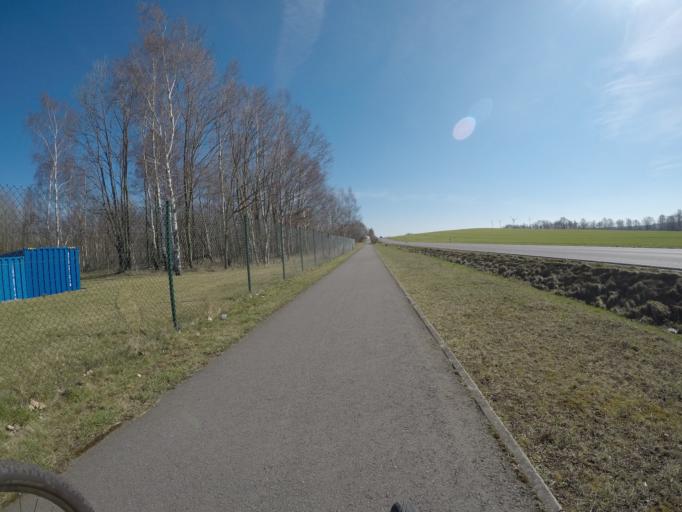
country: DE
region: Saxony
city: Freiberg
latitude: 50.9021
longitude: 13.3653
